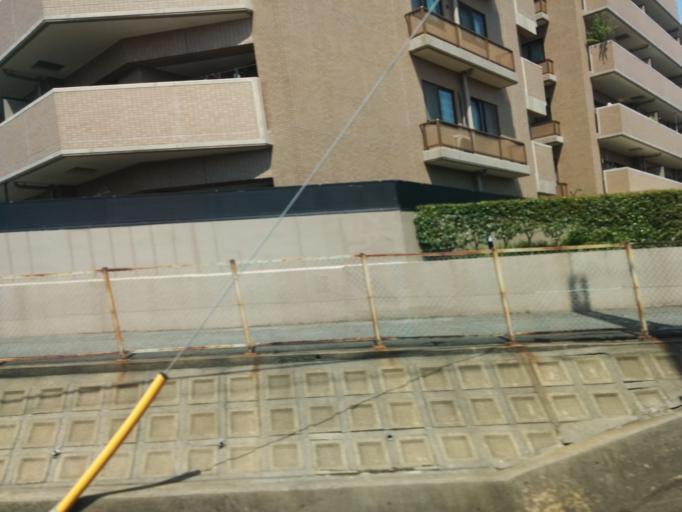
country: JP
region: Osaka
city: Ibaraki
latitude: 34.8336
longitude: 135.5904
